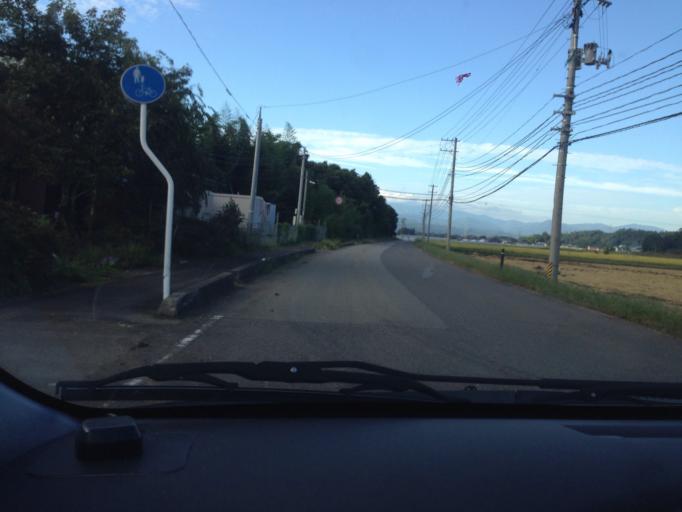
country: JP
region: Fukushima
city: Kitakata
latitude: 37.5831
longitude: 139.7703
